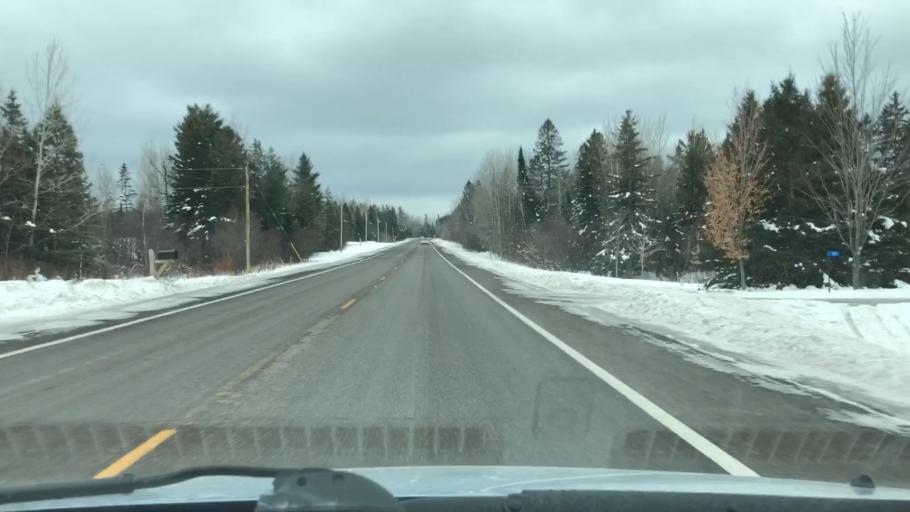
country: US
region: Minnesota
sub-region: Carlton County
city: Esko
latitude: 46.6897
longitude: -92.3648
